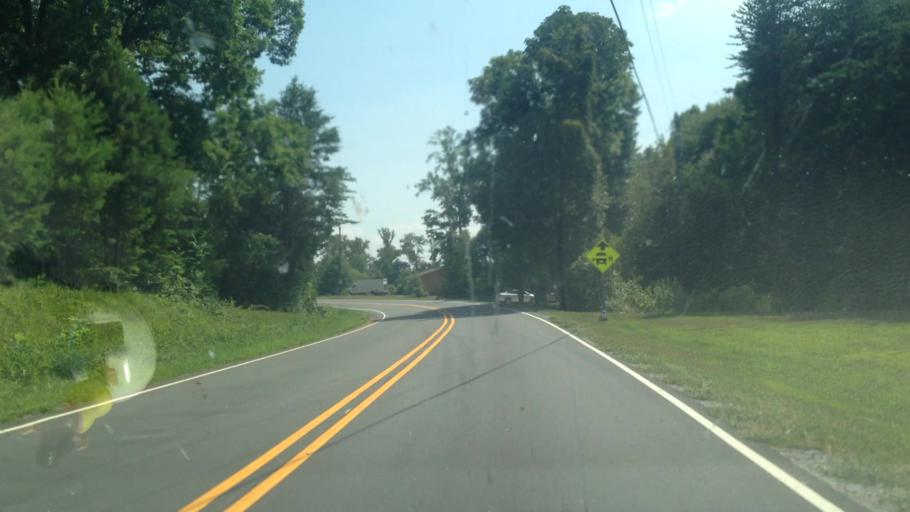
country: US
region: North Carolina
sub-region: Stokes County
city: Danbury
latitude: 36.4091
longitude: -80.0919
